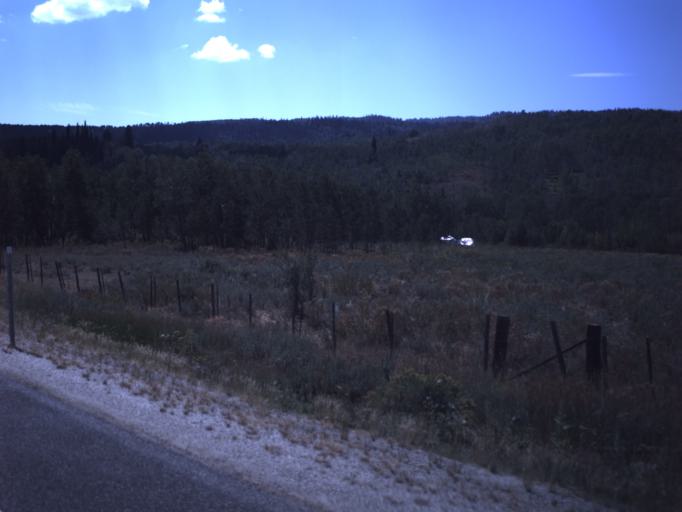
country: US
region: Utah
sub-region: Cache County
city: Richmond
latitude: 41.9210
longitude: -111.5609
